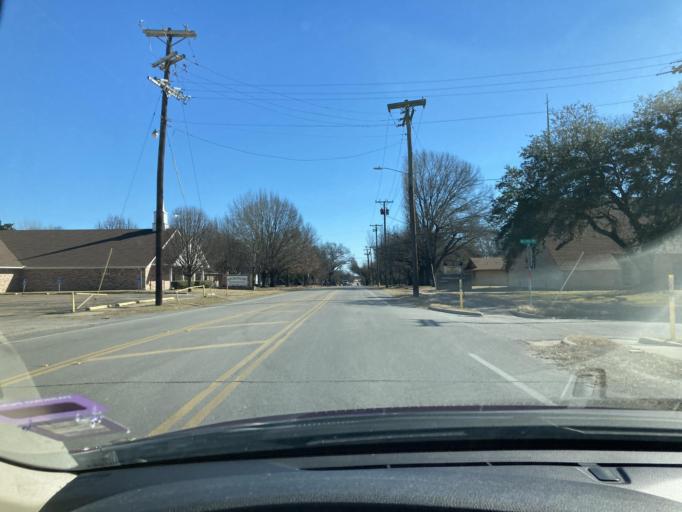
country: US
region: Texas
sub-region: Navarro County
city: Corsicana
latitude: 32.0887
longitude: -96.4675
